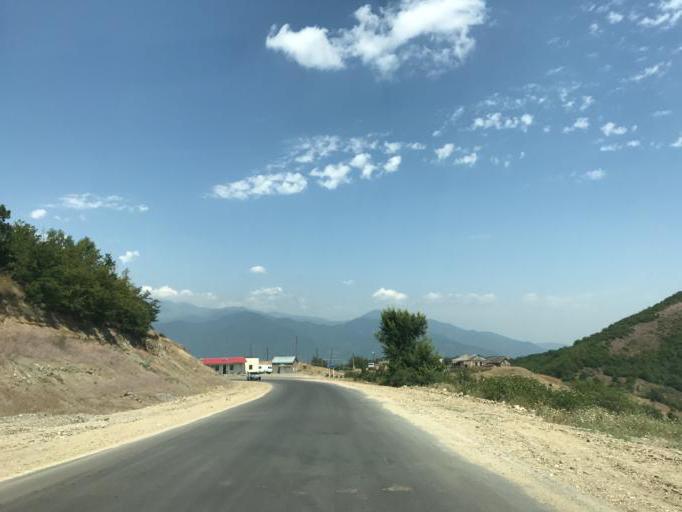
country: AZ
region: Tartar Rayon
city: Martakert
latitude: 40.1286
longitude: 46.6240
